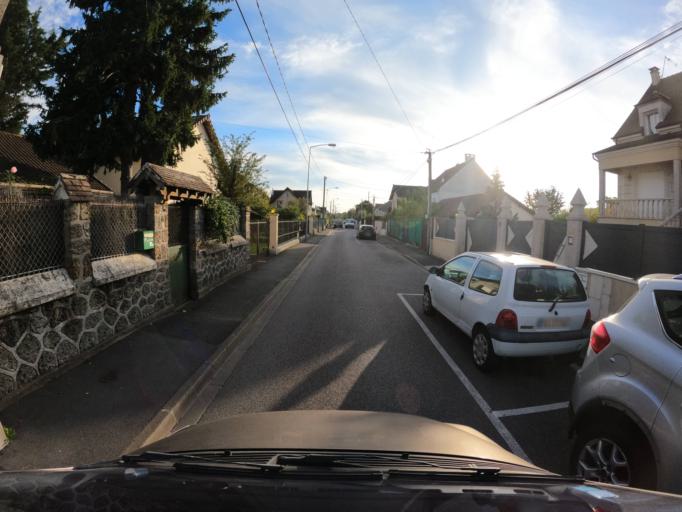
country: FR
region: Ile-de-France
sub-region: Departement de Seine-et-Marne
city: Emerainville
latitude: 48.8022
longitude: 2.6179
